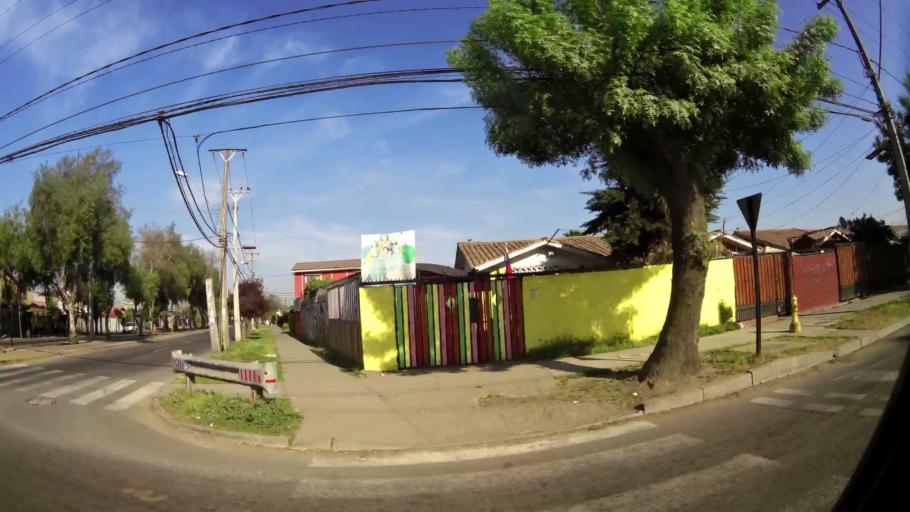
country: CL
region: Santiago Metropolitan
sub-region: Provincia de Santiago
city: Lo Prado
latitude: -33.4609
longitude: -70.7313
